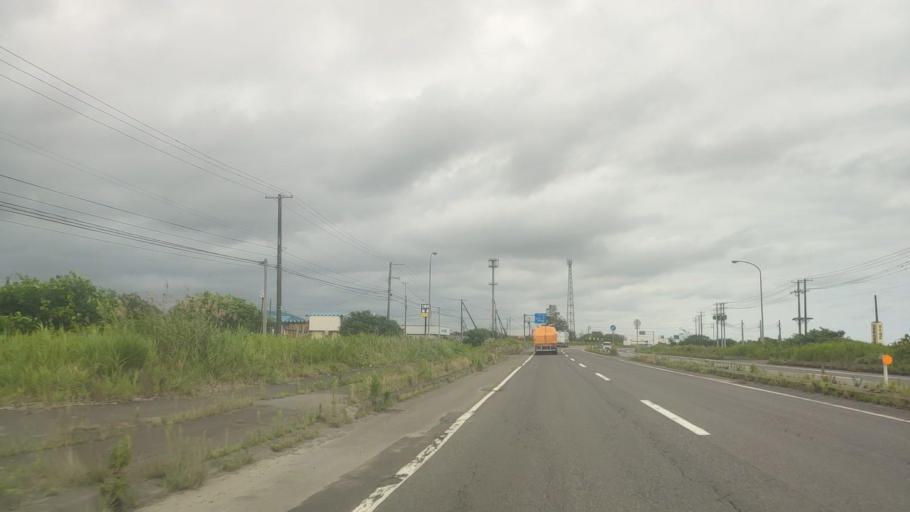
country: JP
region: Hokkaido
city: Shiraoi
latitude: 42.5361
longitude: 141.3312
